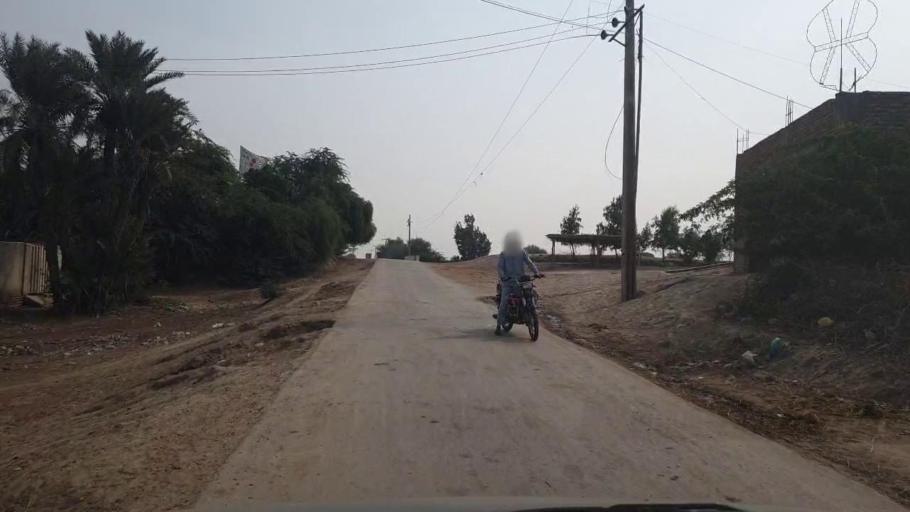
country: PK
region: Sindh
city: Tando Muhammad Khan
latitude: 25.1105
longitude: 68.3633
